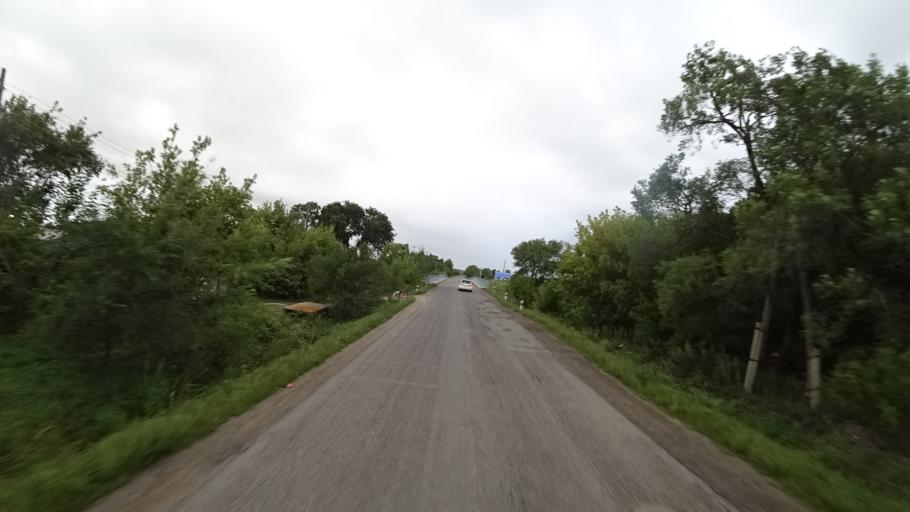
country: RU
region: Primorskiy
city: Chernigovka
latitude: 44.3524
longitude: 132.5682
